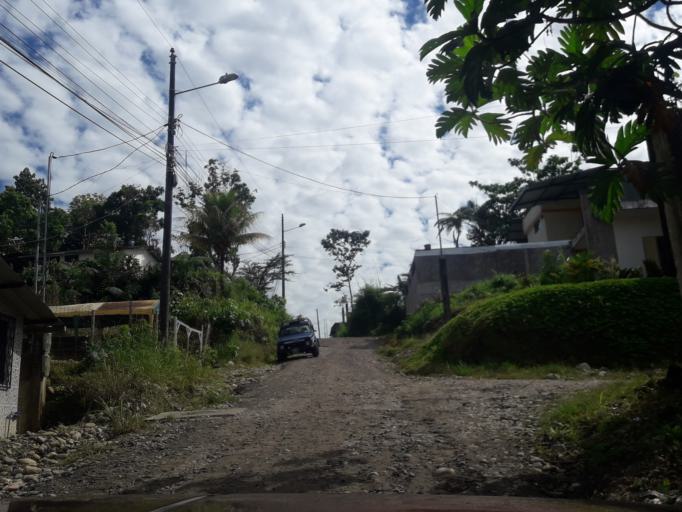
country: EC
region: Napo
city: Tena
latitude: -0.9836
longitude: -77.8192
